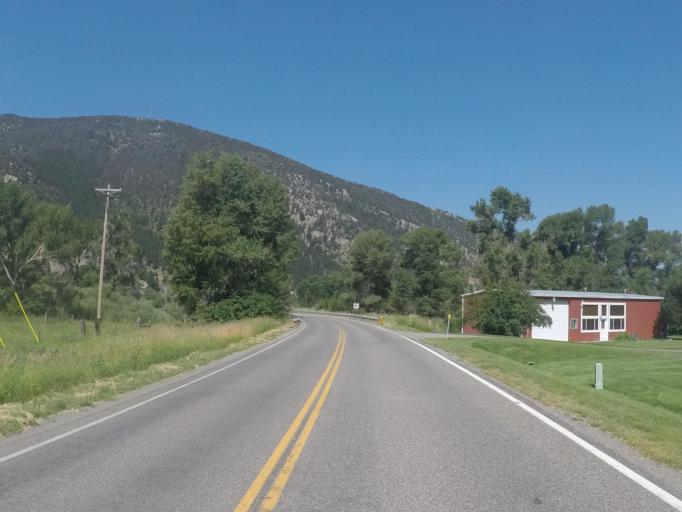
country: US
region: Montana
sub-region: Park County
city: Livingston
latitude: 45.5964
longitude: -110.5643
